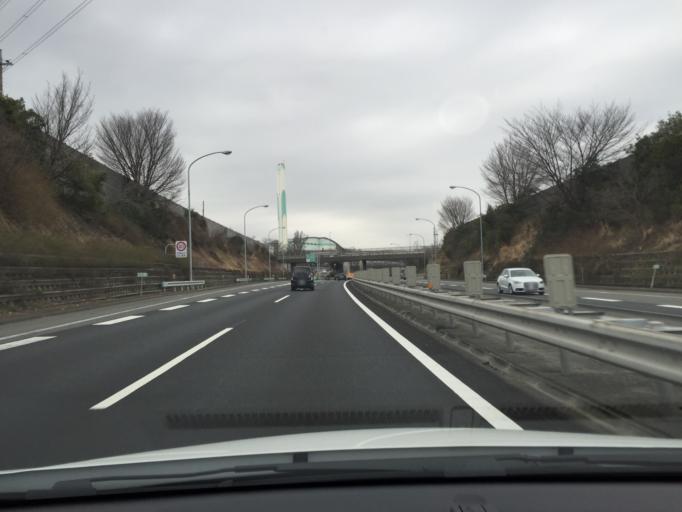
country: JP
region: Saitama
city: Sayama
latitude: 35.8203
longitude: 139.3711
